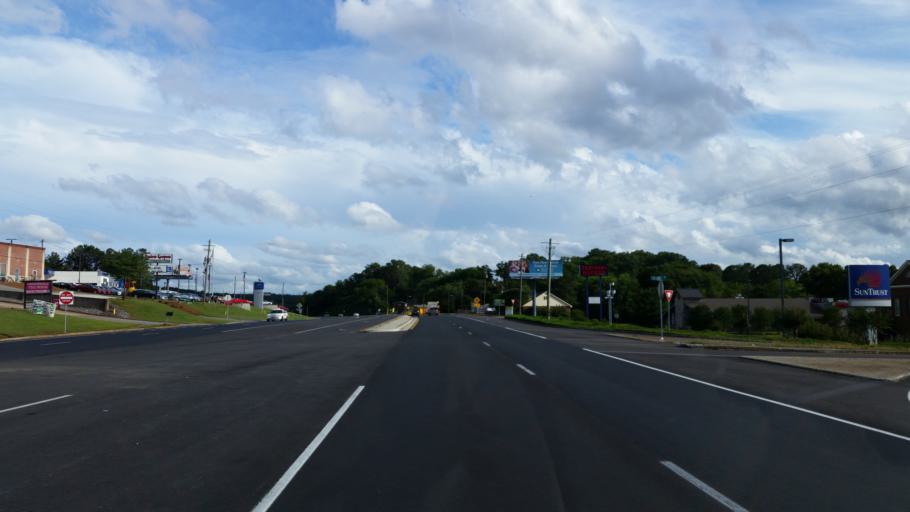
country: US
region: Georgia
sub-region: Bartow County
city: Cartersville
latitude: 34.1933
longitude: -84.7893
